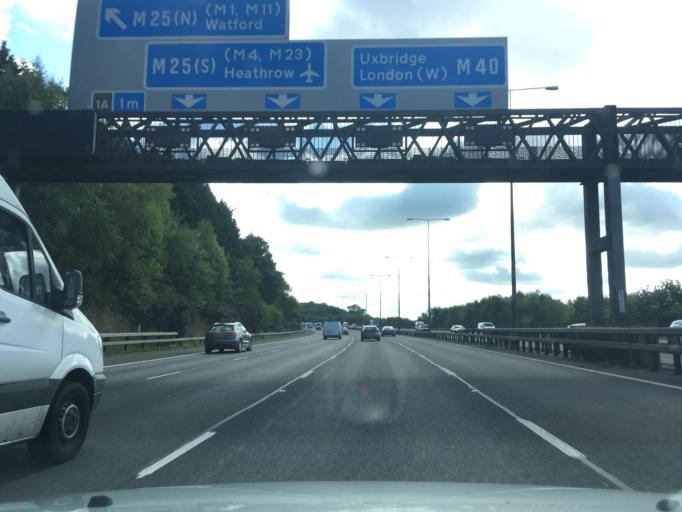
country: GB
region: England
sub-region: Buckinghamshire
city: Gerrards Cross
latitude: 51.5744
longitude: -0.5787
